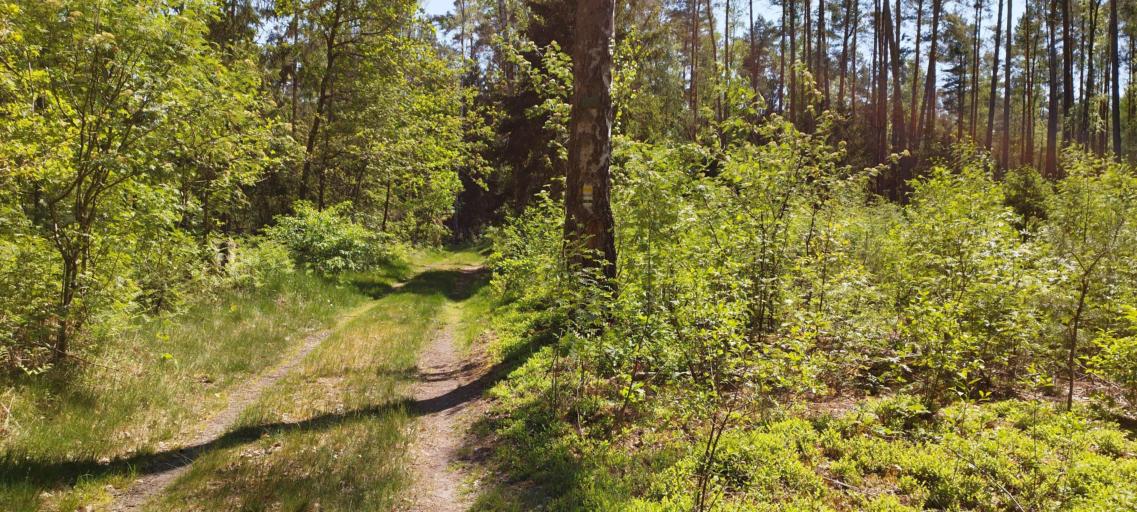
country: DE
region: Brandenburg
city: Rauen
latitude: 52.3834
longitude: 14.0072
